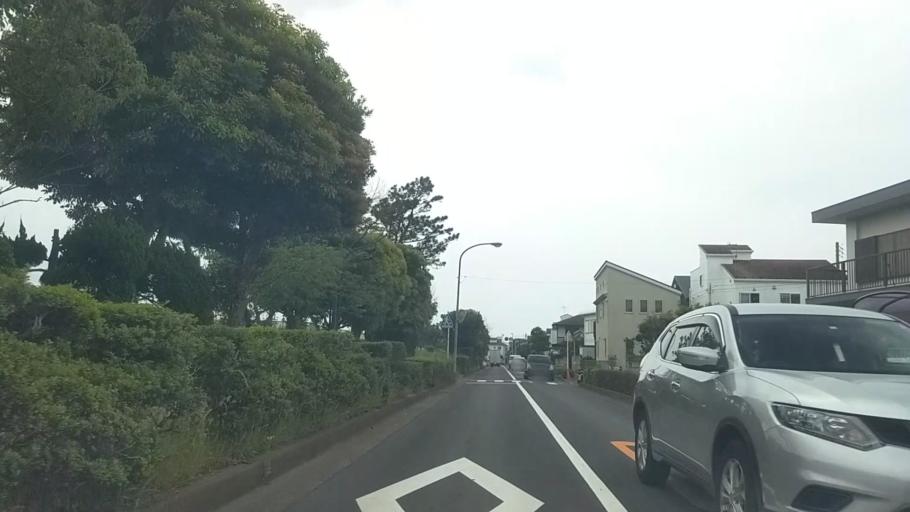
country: JP
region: Kanagawa
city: Fujisawa
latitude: 35.3241
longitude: 139.4621
